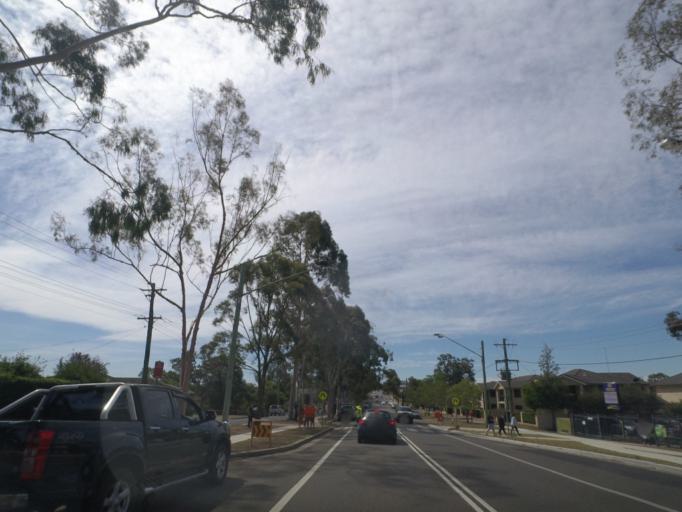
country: AU
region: New South Wales
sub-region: Camden
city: Camden South
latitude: -34.0710
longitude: 150.6944
